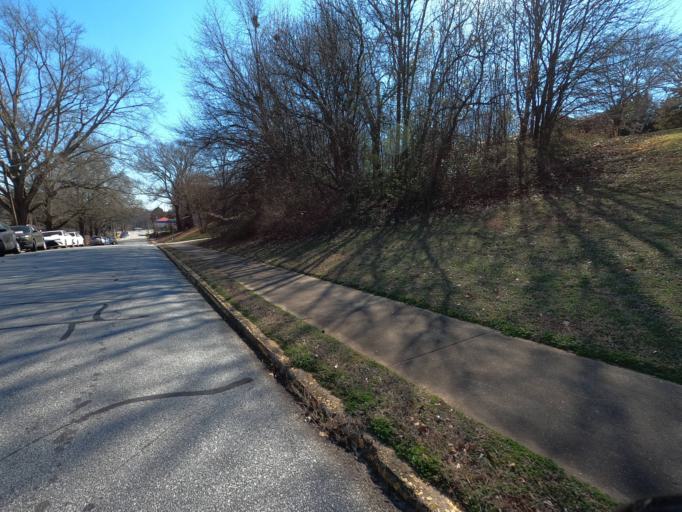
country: US
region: Georgia
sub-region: Clarke County
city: Athens
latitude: 33.9524
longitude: -83.3815
